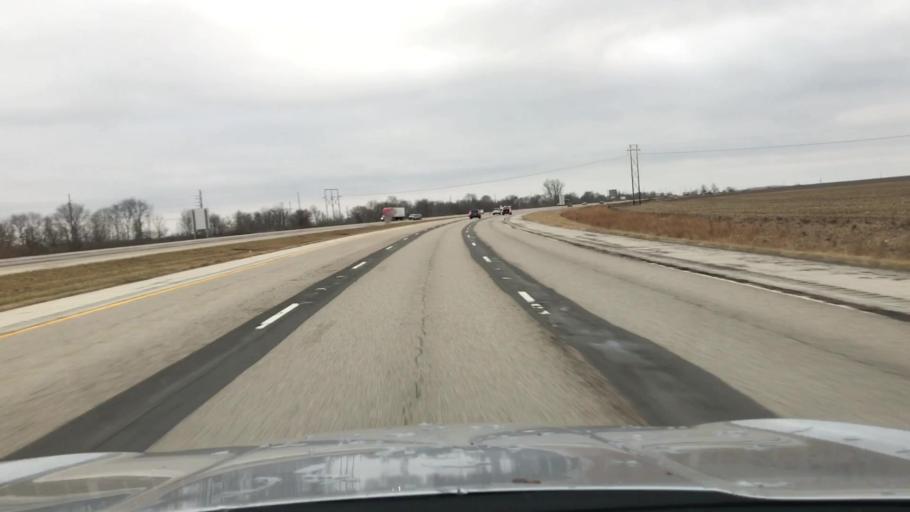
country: US
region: Illinois
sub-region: Logan County
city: Lincoln
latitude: 40.1031
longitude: -89.4166
